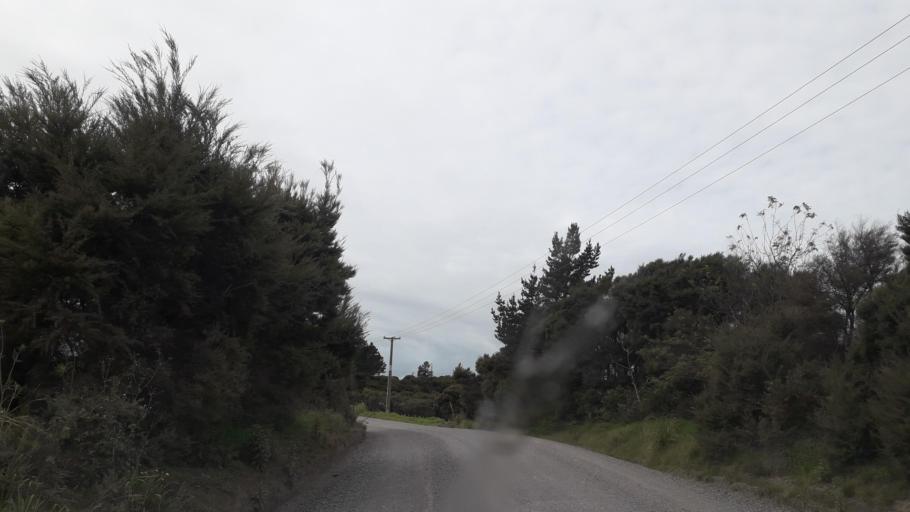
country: NZ
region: Northland
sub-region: Far North District
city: Kerikeri
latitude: -35.1370
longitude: 173.9981
